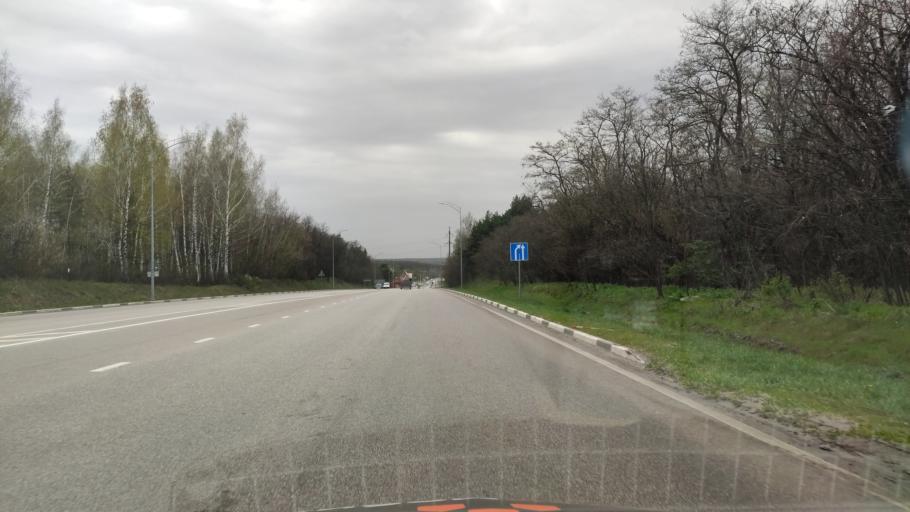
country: RU
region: Belgorod
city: Staryy Oskol
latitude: 51.3599
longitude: 37.8362
